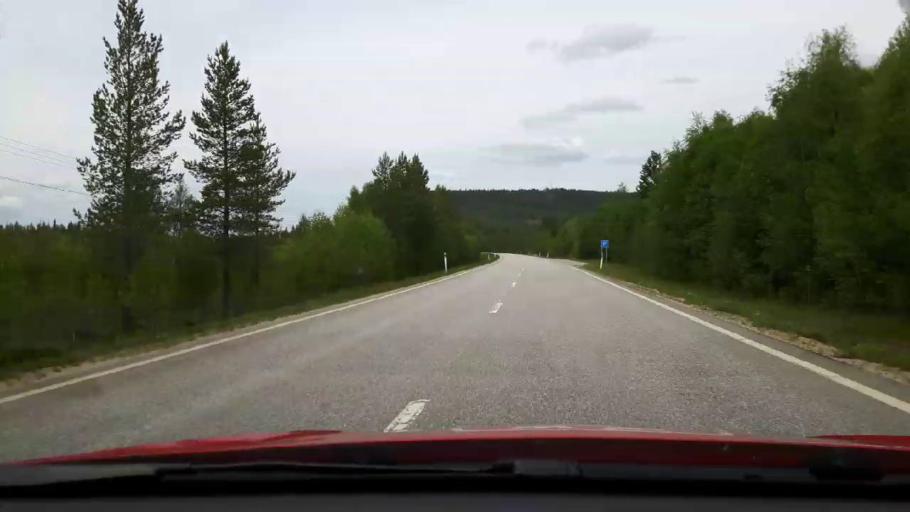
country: SE
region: Jaemtland
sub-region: Harjedalens Kommun
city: Sveg
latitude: 62.0902
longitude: 14.2461
